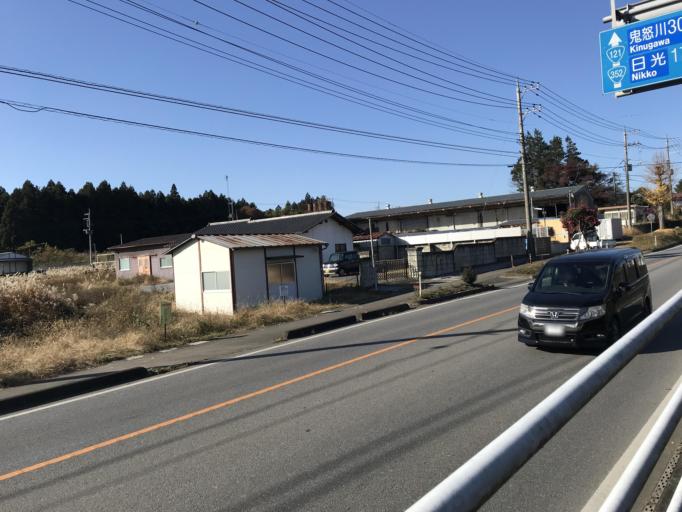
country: JP
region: Tochigi
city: Kanuma
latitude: 36.5878
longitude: 139.7486
